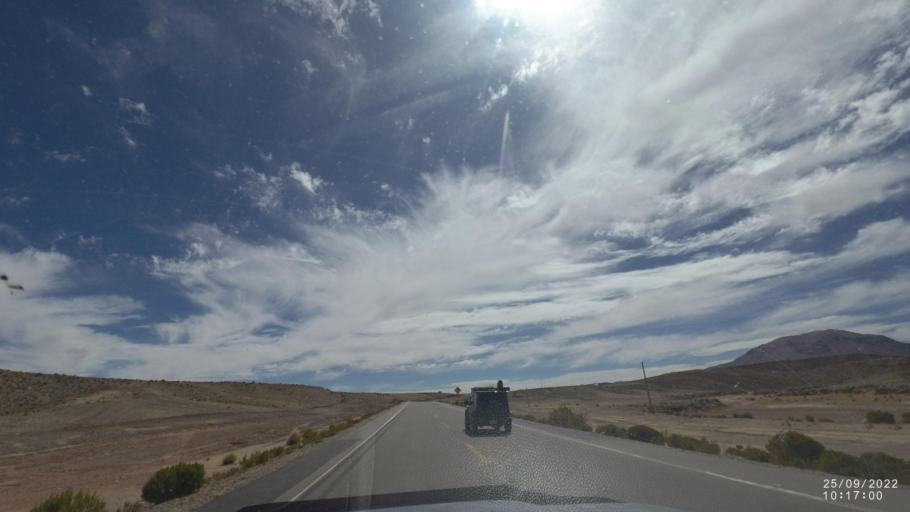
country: BO
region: Potosi
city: Colchani
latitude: -20.0220
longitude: -66.8684
